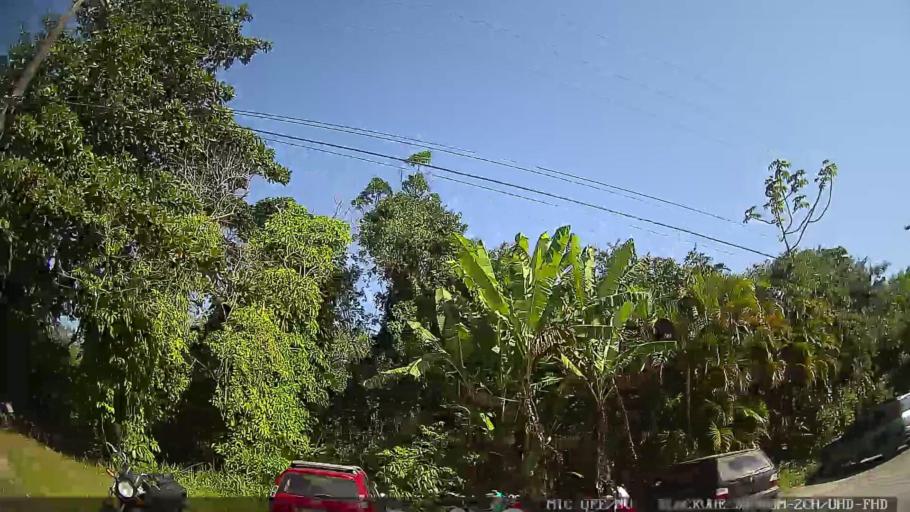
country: BR
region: Sao Paulo
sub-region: Guaruja
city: Guaruja
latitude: -24.0044
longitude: -46.2986
